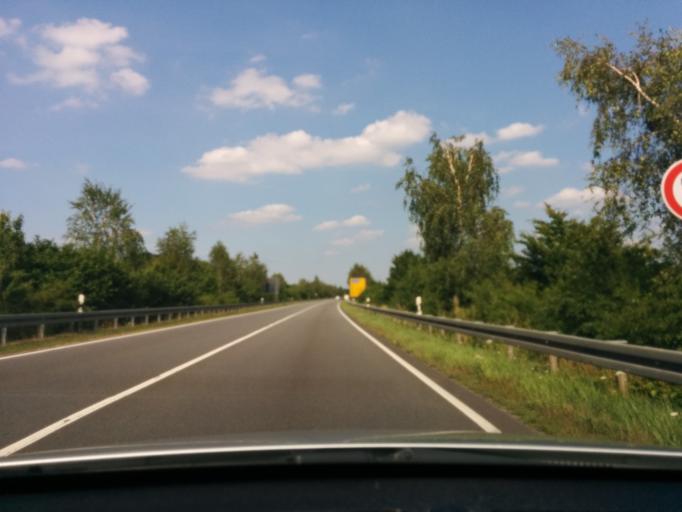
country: DE
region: North Rhine-Westphalia
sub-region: Regierungsbezirk Munster
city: Neuenkirchen
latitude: 52.2249
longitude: 7.3773
